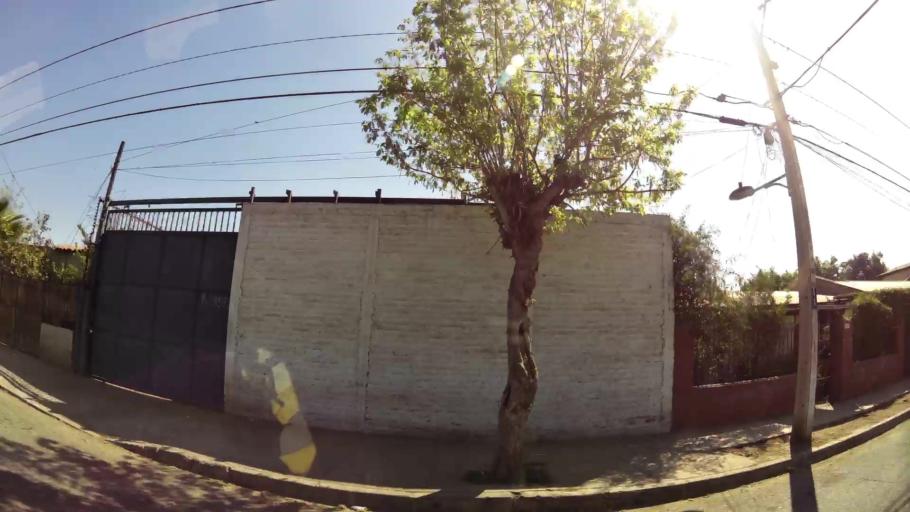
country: CL
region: Santiago Metropolitan
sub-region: Provincia de Santiago
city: La Pintana
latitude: -33.5449
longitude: -70.6091
